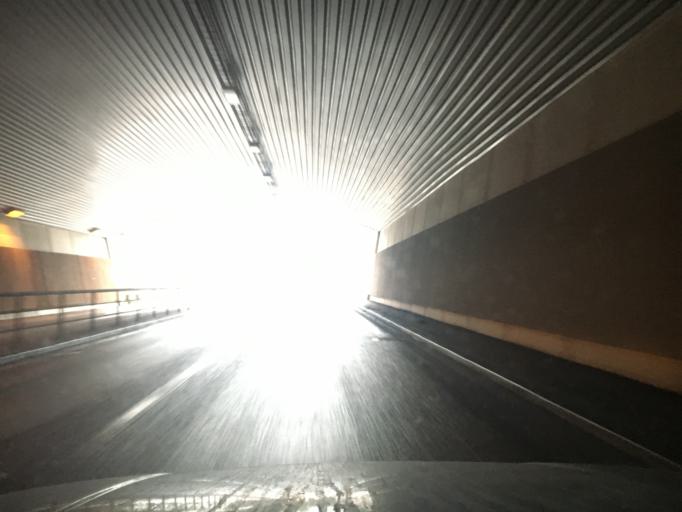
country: FI
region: Uusimaa
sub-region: Helsinki
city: Espoo
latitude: 60.1579
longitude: 24.6609
